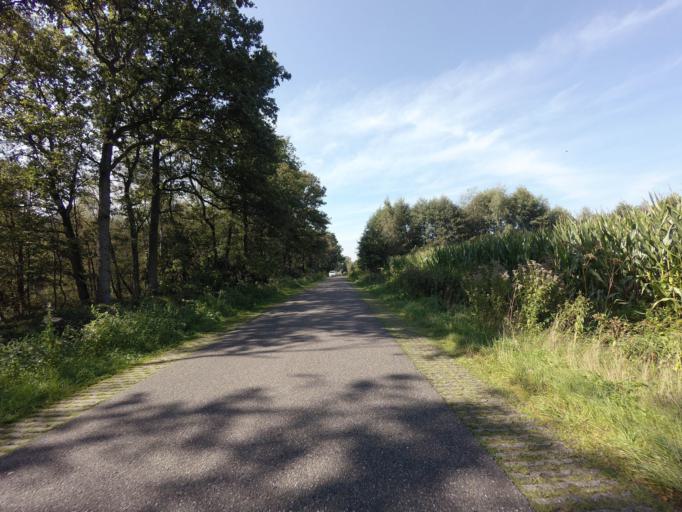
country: NL
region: Overijssel
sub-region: Gemeente Hof van Twente
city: Hengevelde
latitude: 52.2243
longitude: 6.6720
